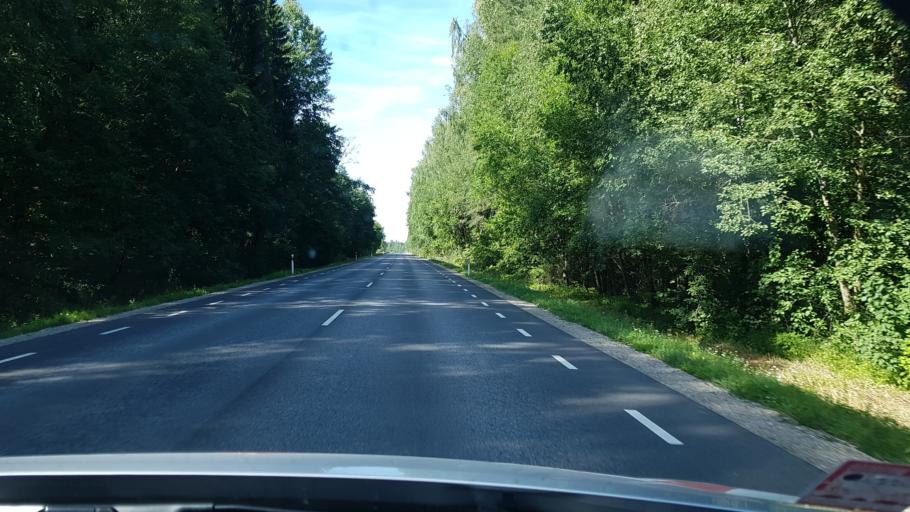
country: EE
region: Polvamaa
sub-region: Polva linn
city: Polva
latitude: 58.0308
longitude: 27.1497
